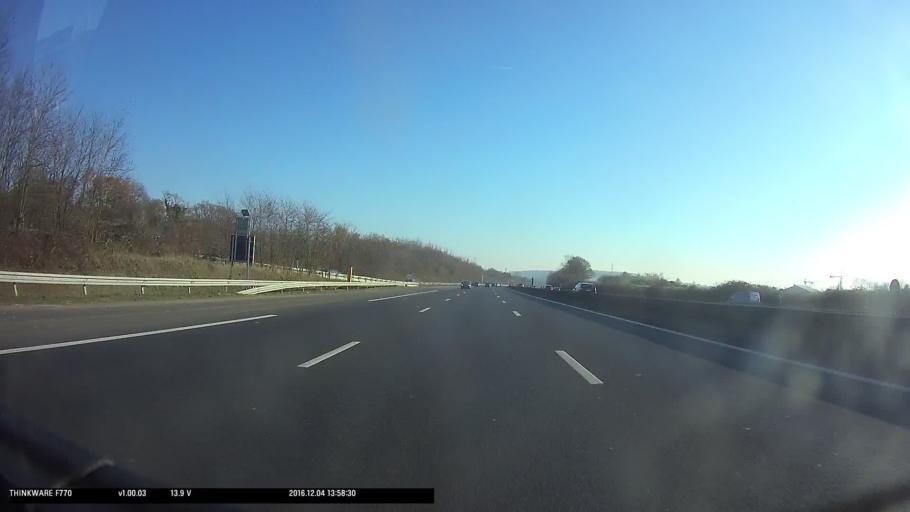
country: FR
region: Ile-de-France
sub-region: Departement du Val-d'Oise
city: Pierrelaye
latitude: 49.0087
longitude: 2.1594
